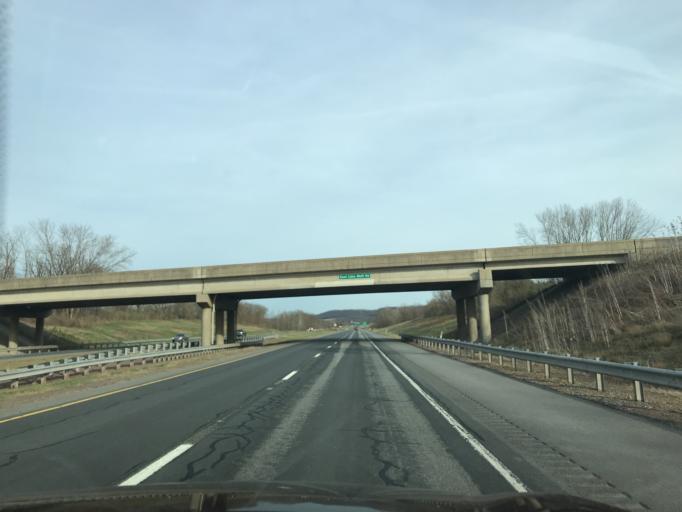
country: US
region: Pennsylvania
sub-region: Lycoming County
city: Muncy
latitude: 41.2226
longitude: -76.7880
